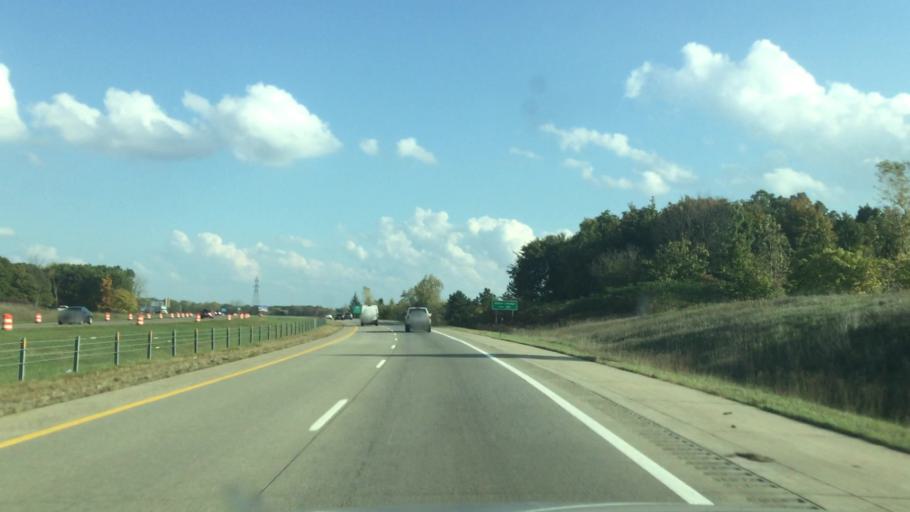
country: US
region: Michigan
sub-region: Calhoun County
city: Albion
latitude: 42.2667
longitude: -84.7749
